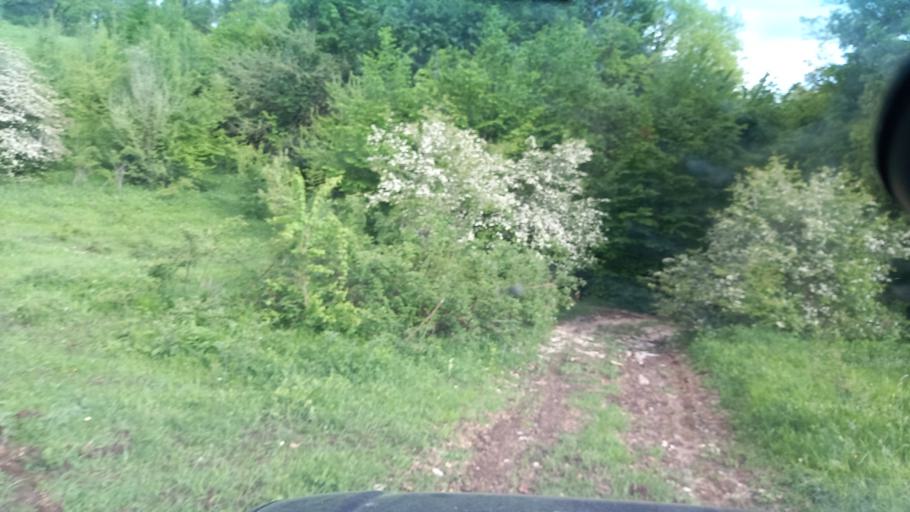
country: RU
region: Adygeya
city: Kamennomostskiy
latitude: 44.2226
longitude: 40.0016
